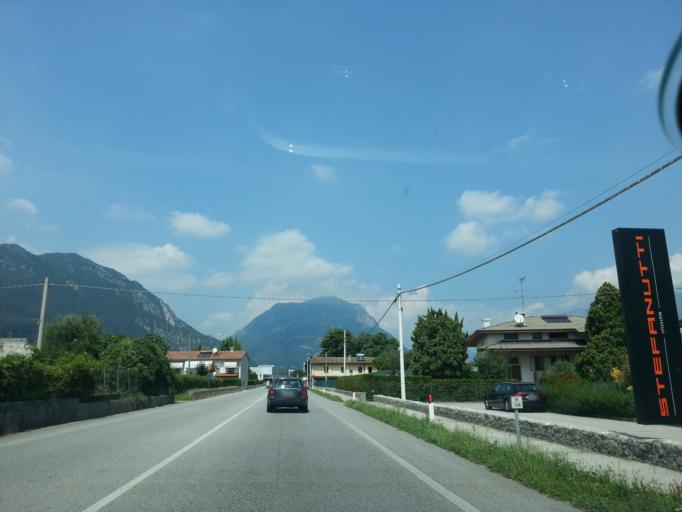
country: IT
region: Friuli Venezia Giulia
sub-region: Provincia di Udine
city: Gemona
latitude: 46.2670
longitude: 13.1076
